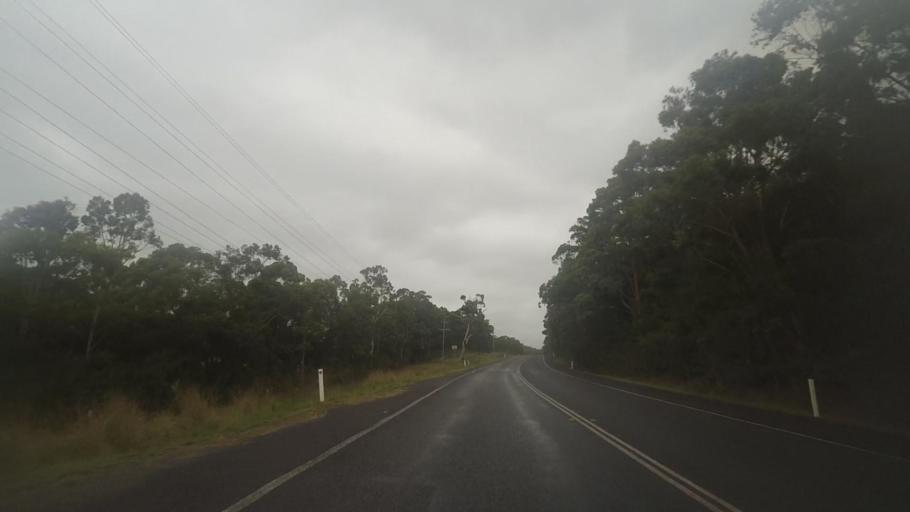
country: AU
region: New South Wales
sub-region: Port Stephens Shire
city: Port Stephens
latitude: -32.6391
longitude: 151.9931
